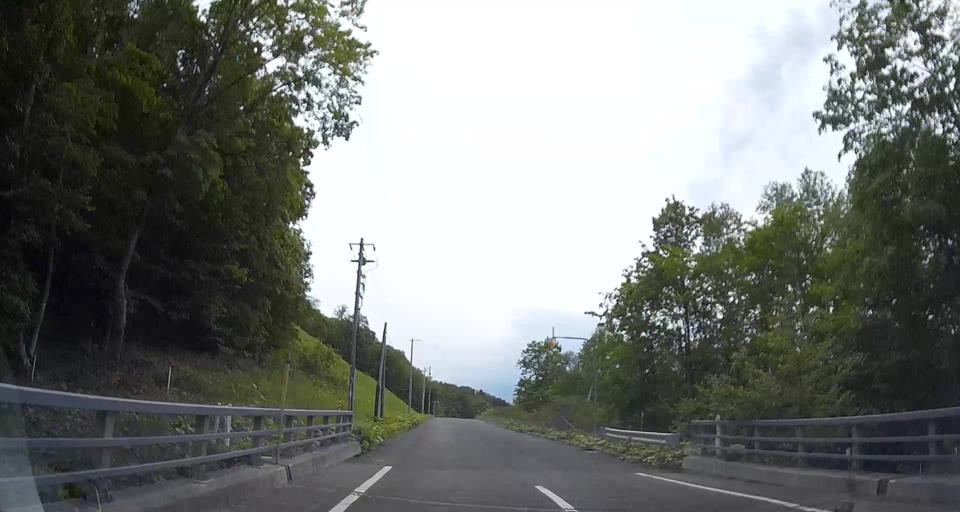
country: JP
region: Hokkaido
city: Chitose
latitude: 42.7740
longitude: 142.0076
